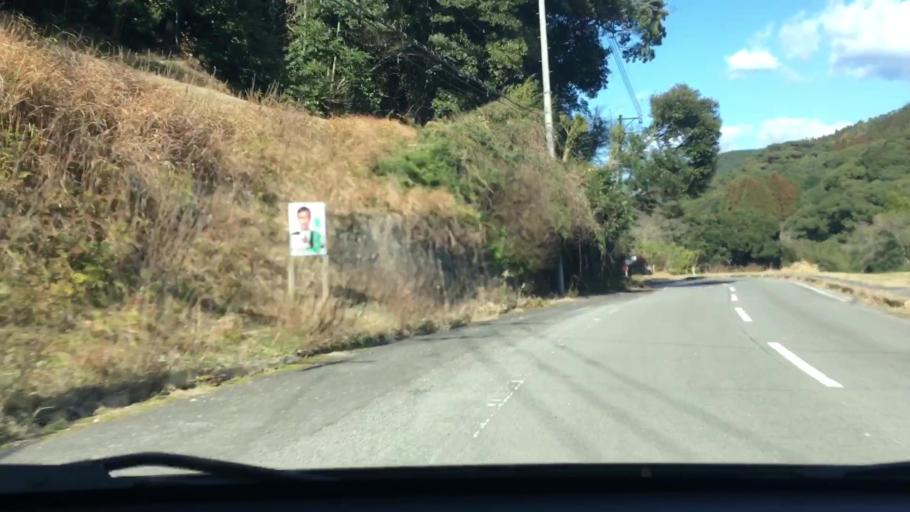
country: JP
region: Kagoshima
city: Ijuin
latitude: 31.7430
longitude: 130.4095
